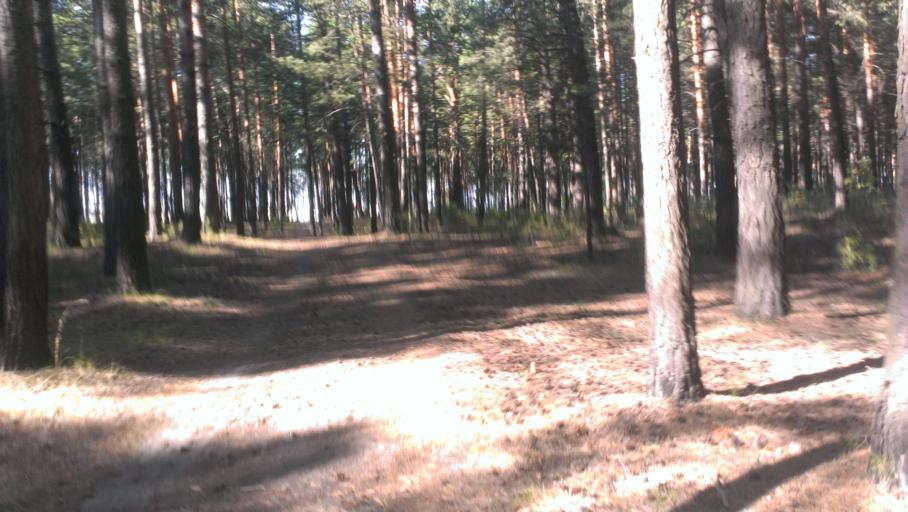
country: RU
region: Altai Krai
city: Novosilikatnyy
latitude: 53.3173
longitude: 83.6836
